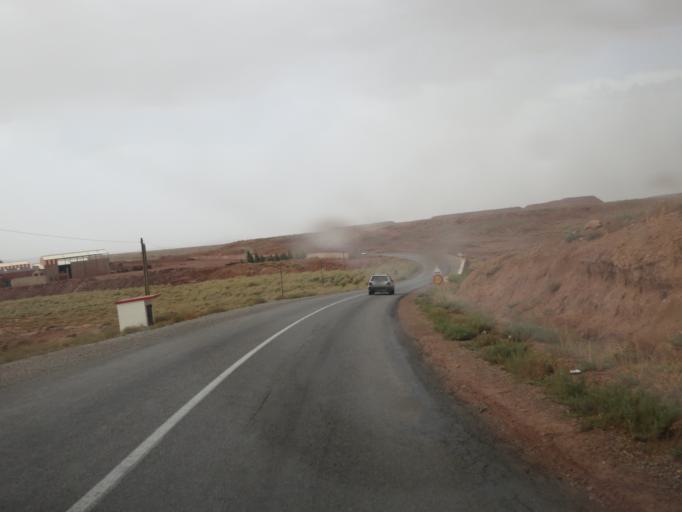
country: MA
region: Meknes-Tafilalet
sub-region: Khenifra
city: Itzer
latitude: 32.8471
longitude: -4.9510
